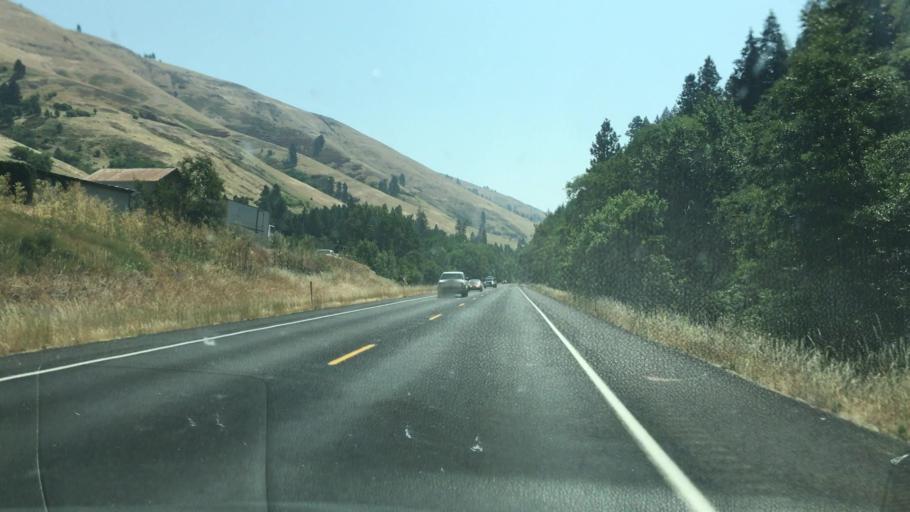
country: US
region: Idaho
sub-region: Nez Perce County
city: Lapwai
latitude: 46.3627
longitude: -116.6374
